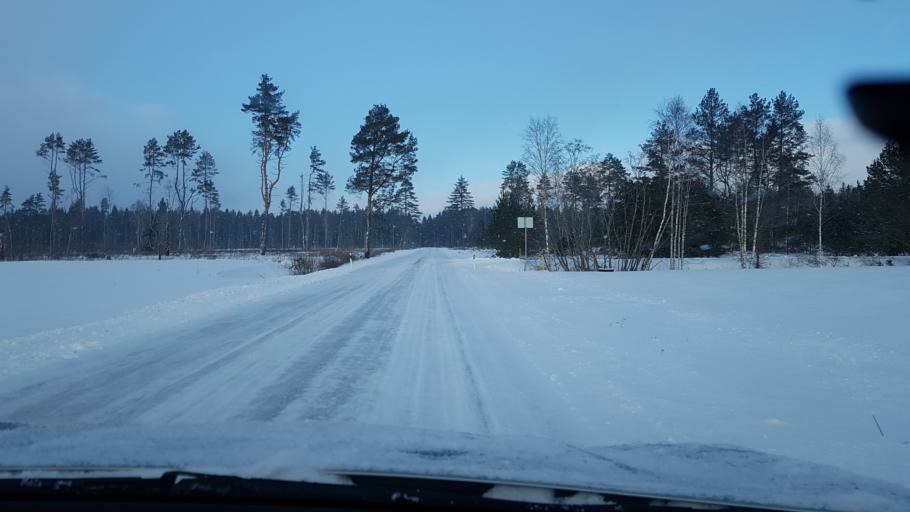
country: EE
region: Harju
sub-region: Nissi vald
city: Turba
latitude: 59.2045
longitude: 24.1404
